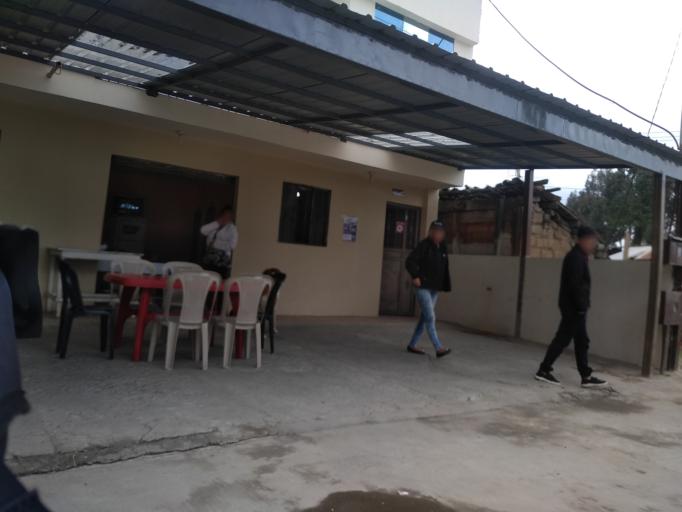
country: EC
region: Loja
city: Loja
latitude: -3.9582
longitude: -79.2427
